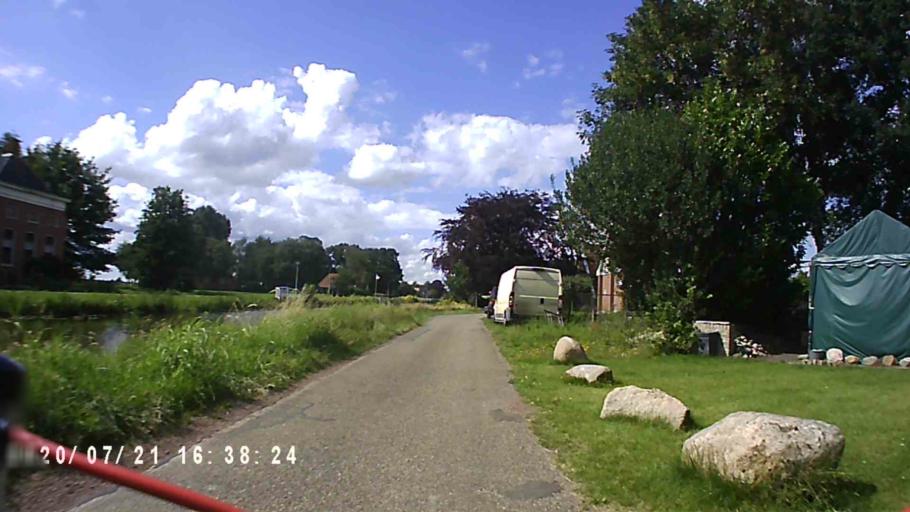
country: NL
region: Groningen
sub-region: Gemeente Hoogezand-Sappemeer
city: Sappemeer
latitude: 53.0924
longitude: 6.7944
